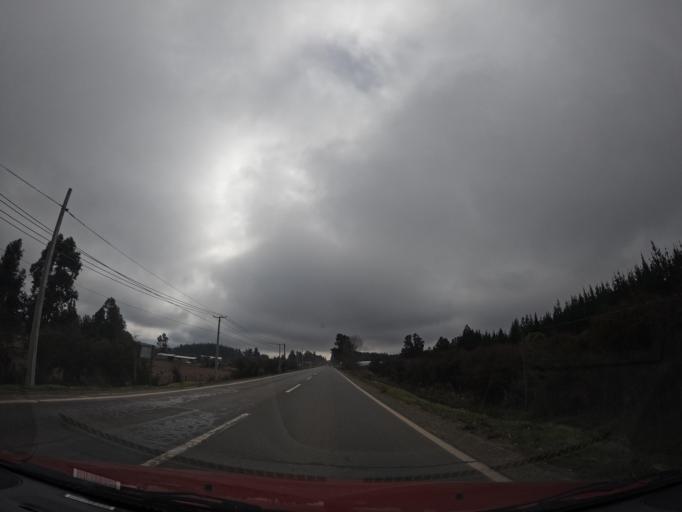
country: CL
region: Maule
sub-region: Provincia de Cauquenes
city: Cauquenes
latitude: -36.2645
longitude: -72.5480
